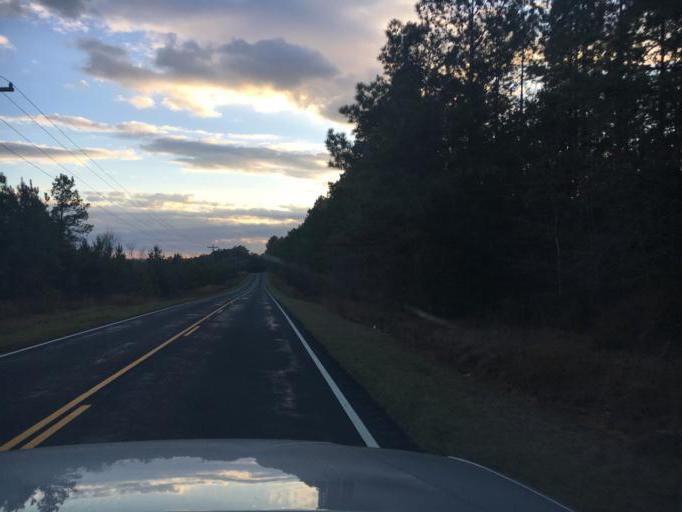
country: US
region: South Carolina
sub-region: Greenwood County
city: Greenwood
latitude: 34.0812
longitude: -82.2125
